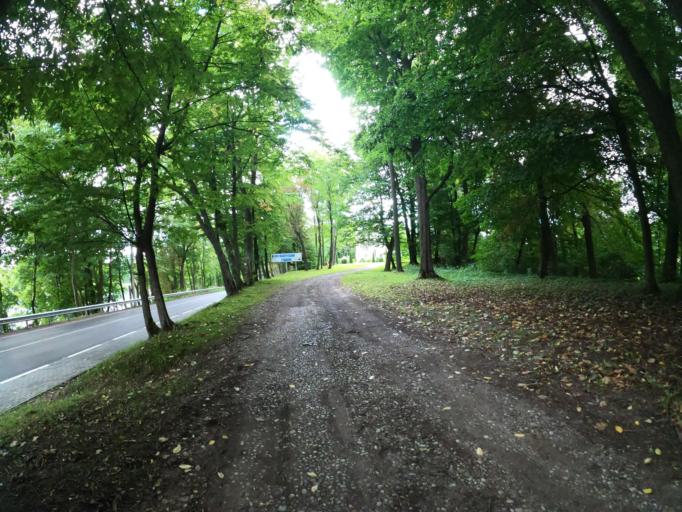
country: RU
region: Kaliningrad
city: Zheleznodorozhnyy
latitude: 54.3619
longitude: 21.3112
